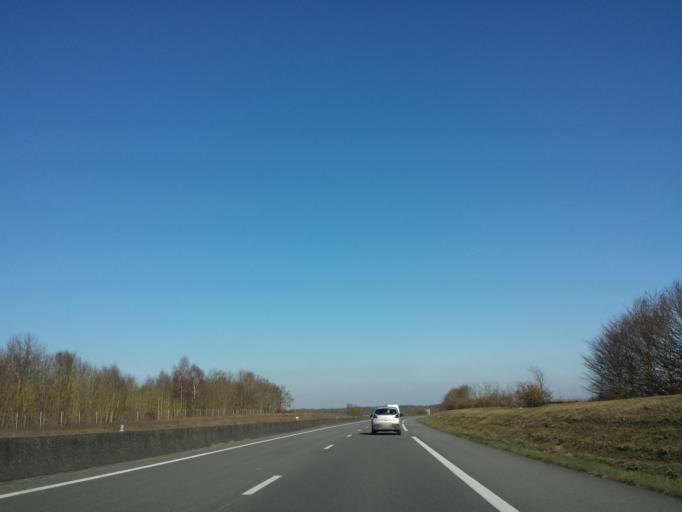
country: FR
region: Picardie
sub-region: Departement de l'Oise
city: Breteuil
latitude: 49.6282
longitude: 2.2085
